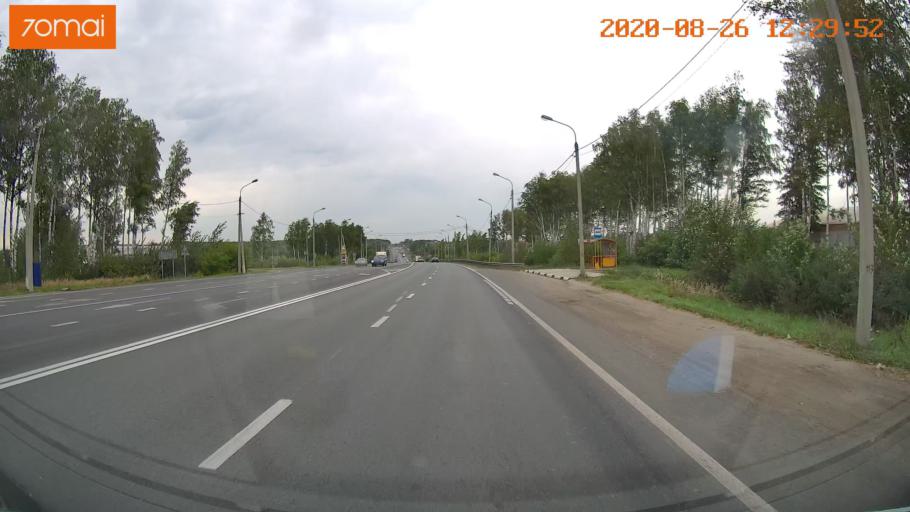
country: RU
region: Rjazan
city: Ryazan'
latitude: 54.5667
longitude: 39.8115
